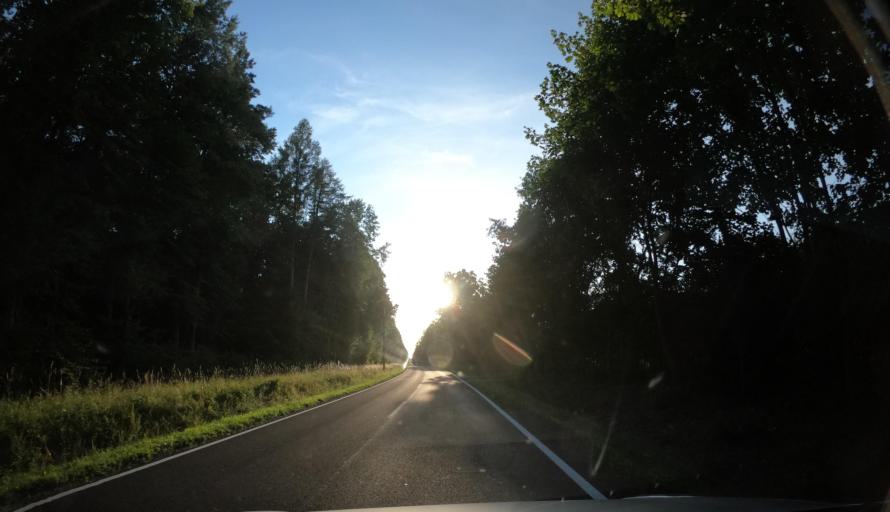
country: PL
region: Kujawsko-Pomorskie
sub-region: Powiat swiecki
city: Swiekatowo
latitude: 53.3069
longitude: 18.0605
